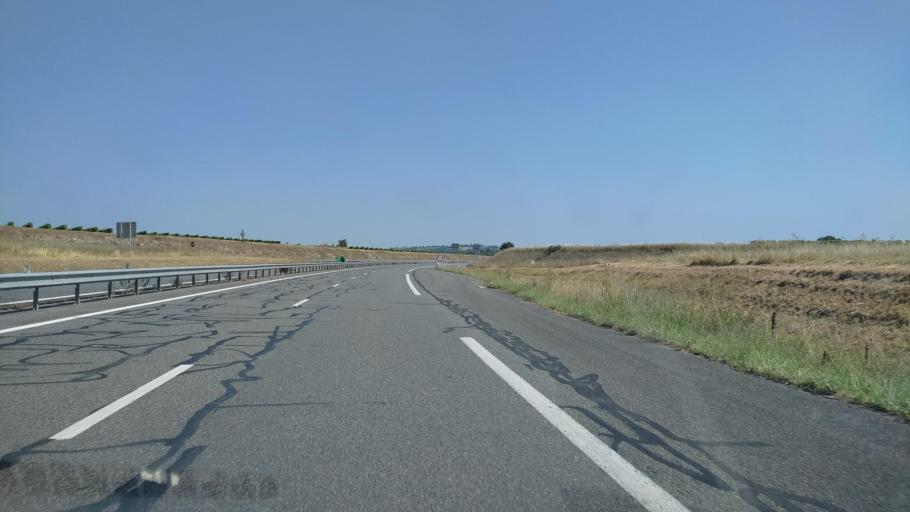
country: FR
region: Poitou-Charentes
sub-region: Departement de la Charente
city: Saint-Meme-les-Carrieres
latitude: 45.6911
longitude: -0.0866
